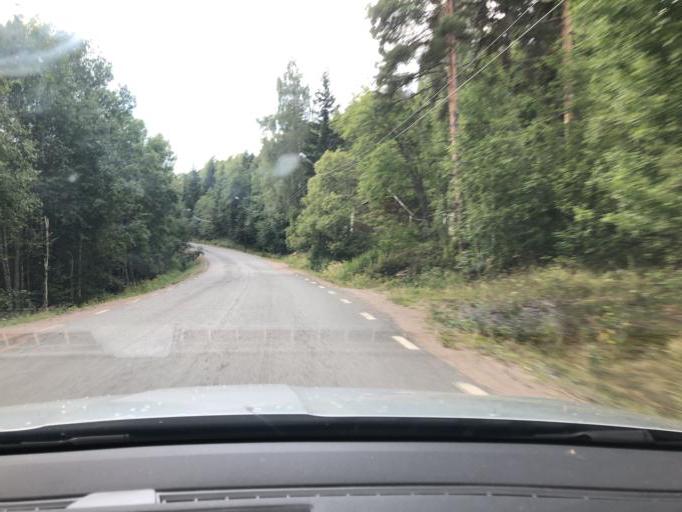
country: SE
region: Vaesternorrland
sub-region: Solleftea Kommun
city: Solleftea
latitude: 63.2111
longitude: 17.1774
